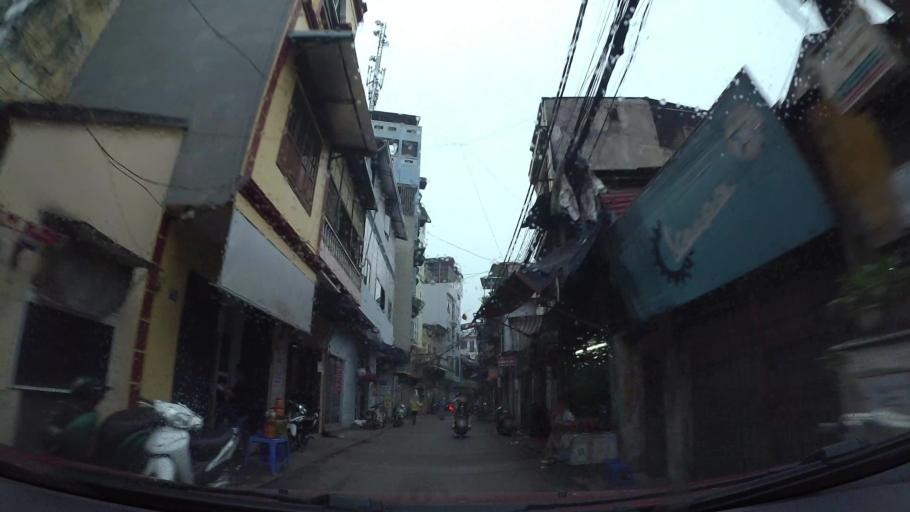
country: VN
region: Ha Noi
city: Hanoi
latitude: 21.0222
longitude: 105.8391
